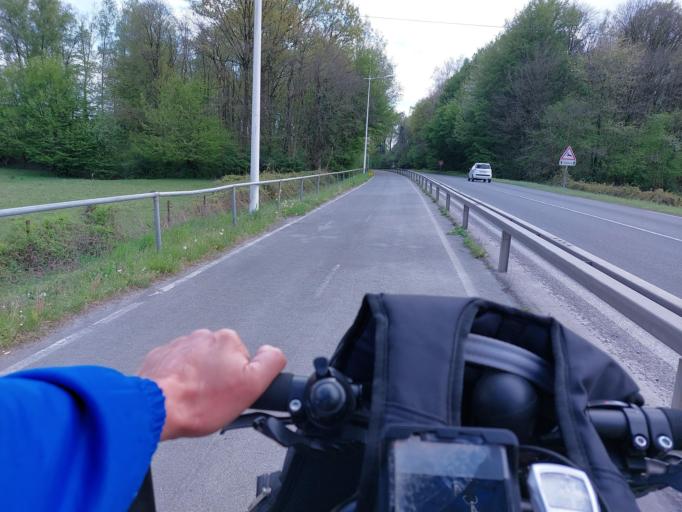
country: FR
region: Nord-Pas-de-Calais
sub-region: Departement du Nord
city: Hautmont
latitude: 50.2581
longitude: 3.8962
